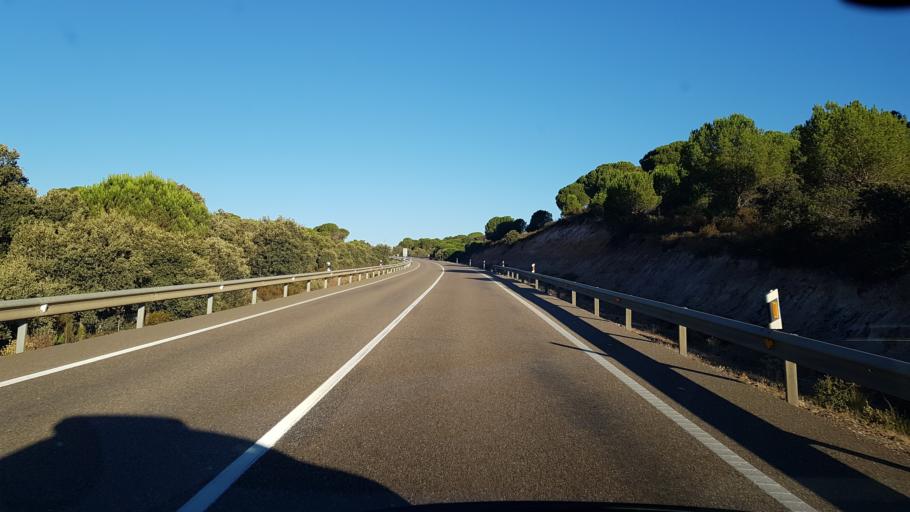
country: ES
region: Castille and Leon
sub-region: Provincia de Zamora
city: Palacios del Pan
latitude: 41.5383
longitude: -5.8464
